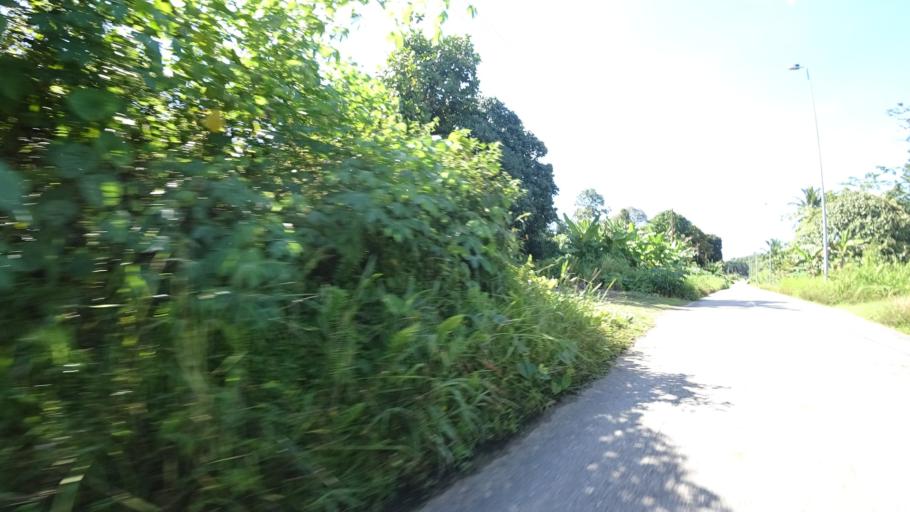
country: BN
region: Tutong
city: Tutong
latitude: 4.7389
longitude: 114.7906
